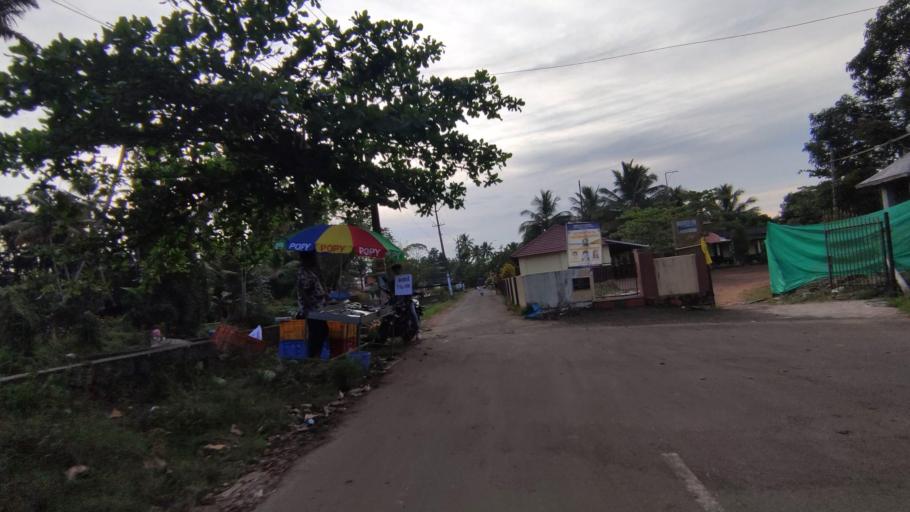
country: IN
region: Kerala
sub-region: Kottayam
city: Kottayam
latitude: 9.6447
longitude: 76.4797
